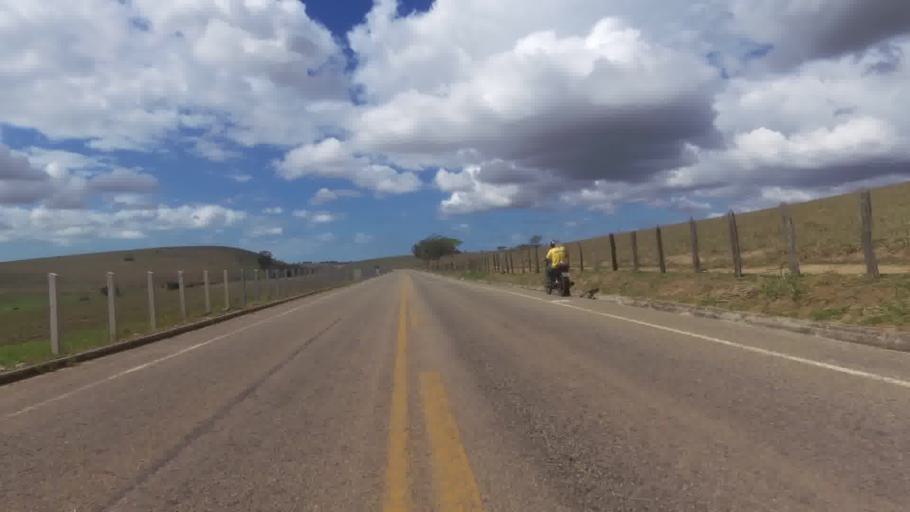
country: BR
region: Espirito Santo
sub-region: Marataizes
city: Marataizes
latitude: -21.1266
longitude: -41.0135
